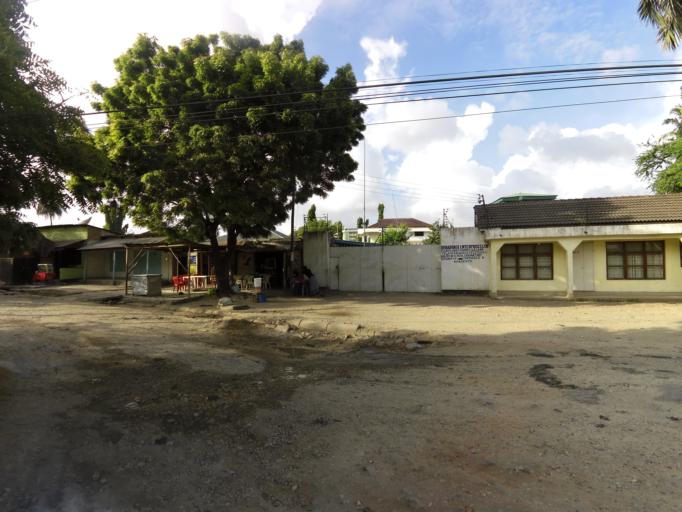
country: TZ
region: Dar es Salaam
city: Magomeni
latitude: -6.7743
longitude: 39.2405
